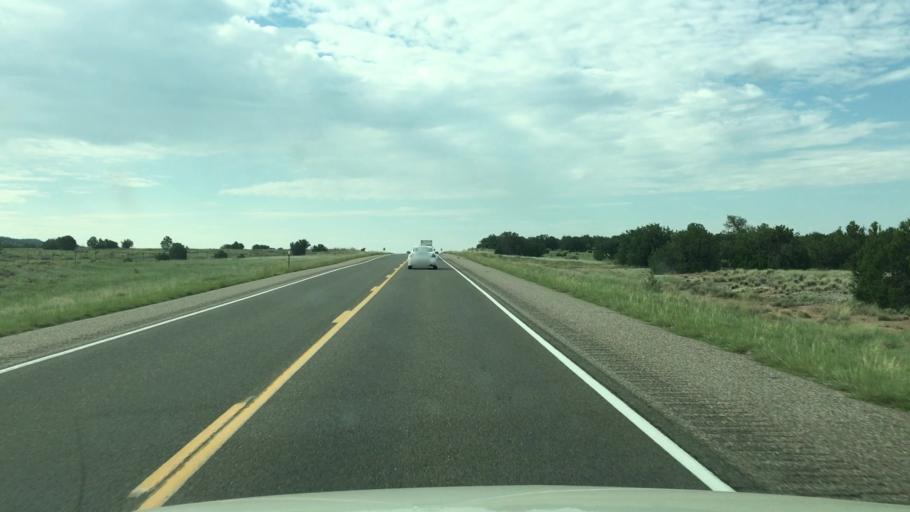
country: US
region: New Mexico
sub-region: Santa Fe County
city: Eldorado at Santa Fe
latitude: 35.3150
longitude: -105.8306
